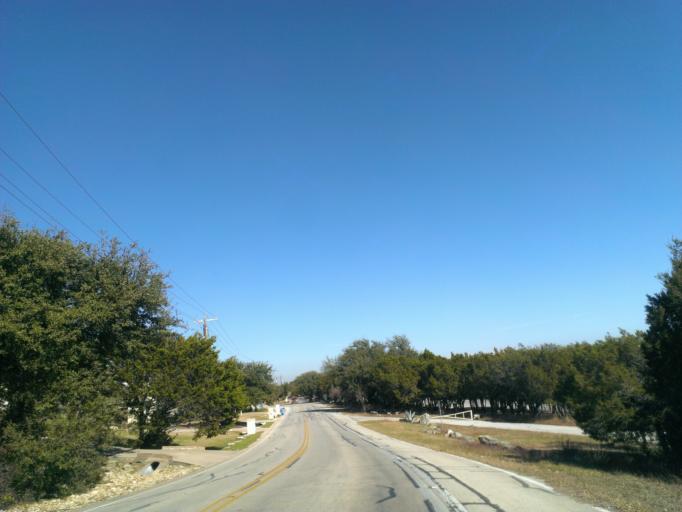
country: US
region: Texas
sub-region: Travis County
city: Lakeway
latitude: 30.3783
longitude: -97.9690
